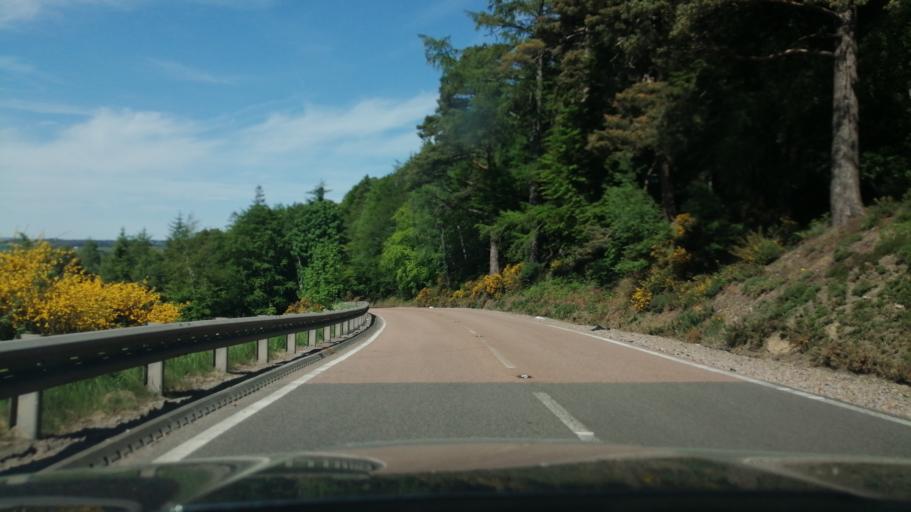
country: GB
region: Scotland
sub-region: Moray
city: Rothes
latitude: 57.4890
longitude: -3.1706
